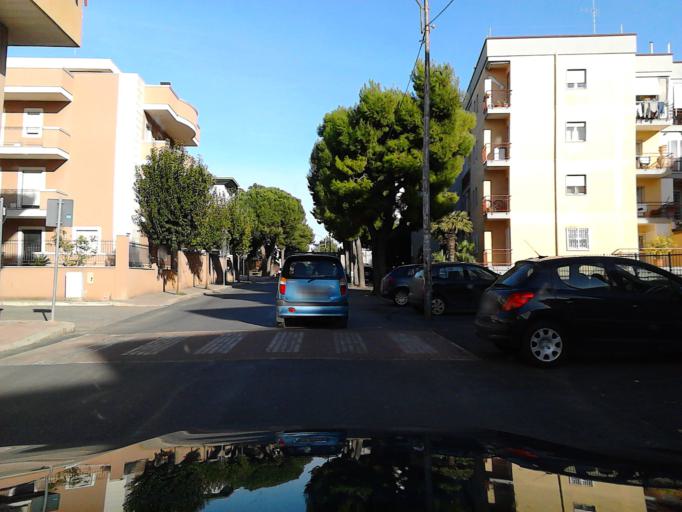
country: IT
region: Apulia
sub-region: Provincia di Bari
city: Rutigliano
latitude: 41.0119
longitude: 17.0109
